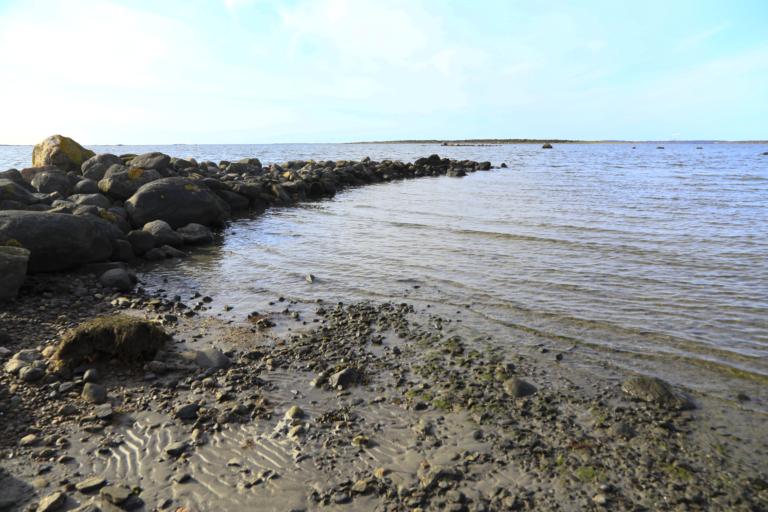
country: SE
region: Halland
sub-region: Varbergs Kommun
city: Varberg
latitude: 57.1299
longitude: 12.2111
